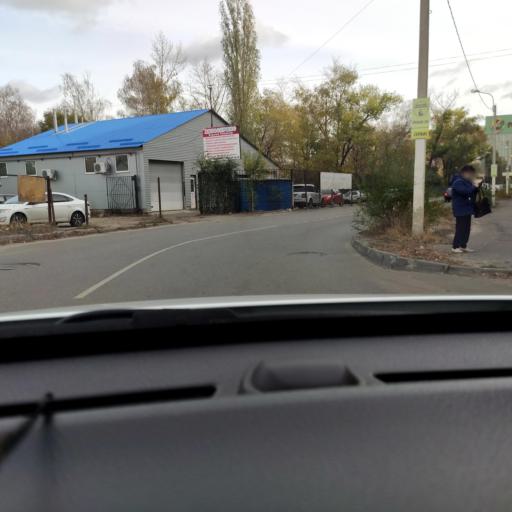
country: RU
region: Voronezj
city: Voronezh
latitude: 51.6983
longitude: 39.2694
